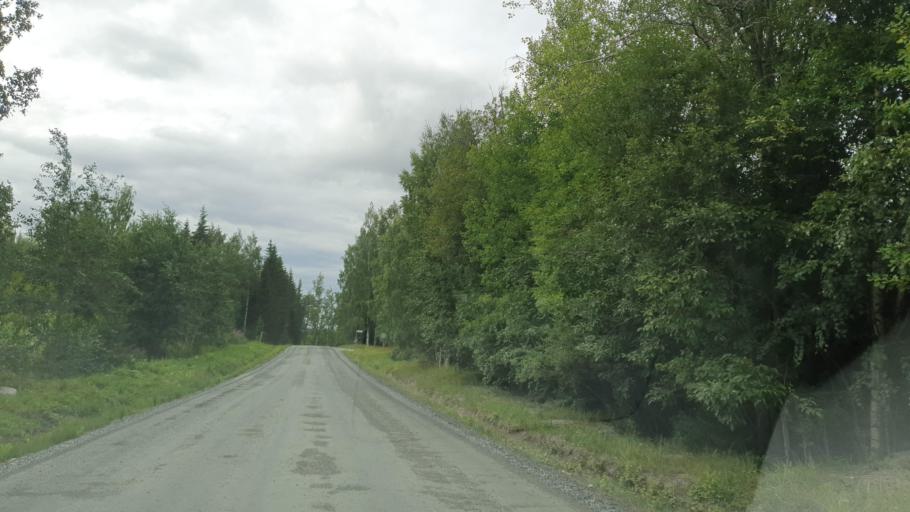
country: FI
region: Northern Savo
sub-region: Ylae-Savo
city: Iisalmi
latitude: 63.5176
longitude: 27.1046
